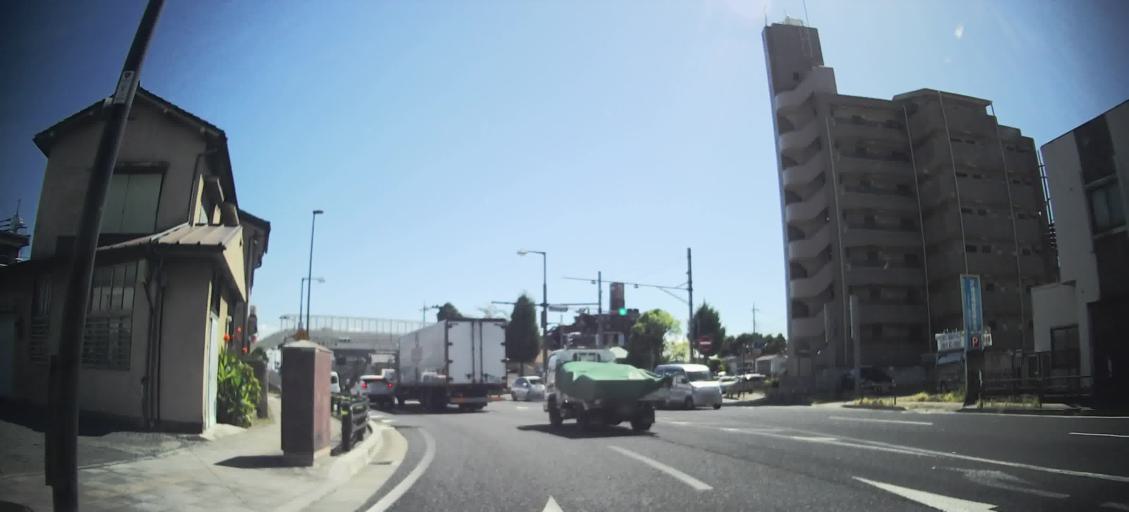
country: JP
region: Gunma
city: Maebashi-shi
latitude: 36.3859
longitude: 139.0768
